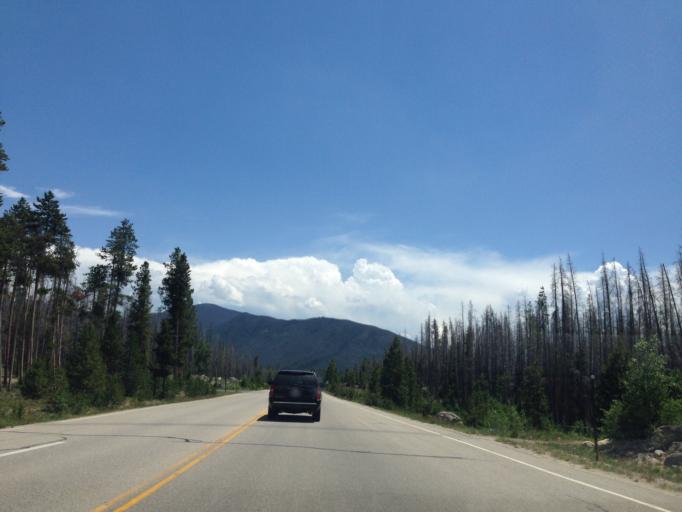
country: US
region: Colorado
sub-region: Grand County
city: Granby
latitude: 40.2664
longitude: -105.8335
